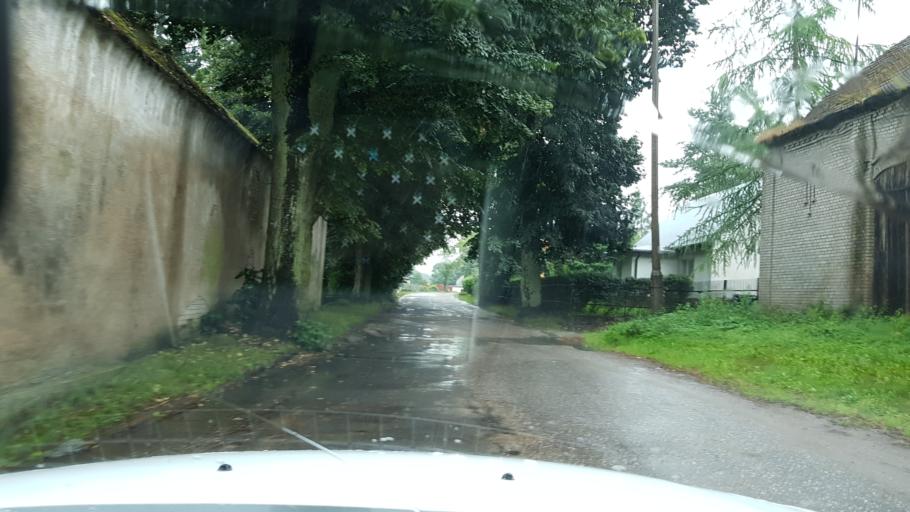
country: PL
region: West Pomeranian Voivodeship
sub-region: Powiat kolobrzeski
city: Ryman
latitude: 53.9683
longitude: 15.4547
